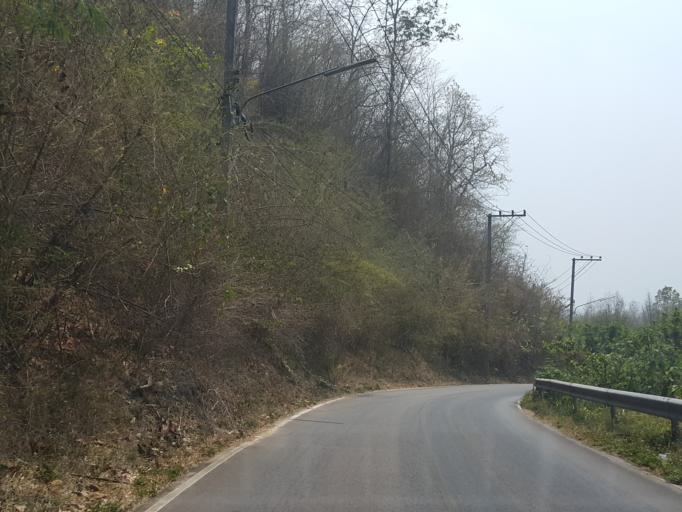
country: TH
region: Chiang Mai
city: Mae Taeng
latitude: 19.0013
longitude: 98.8884
